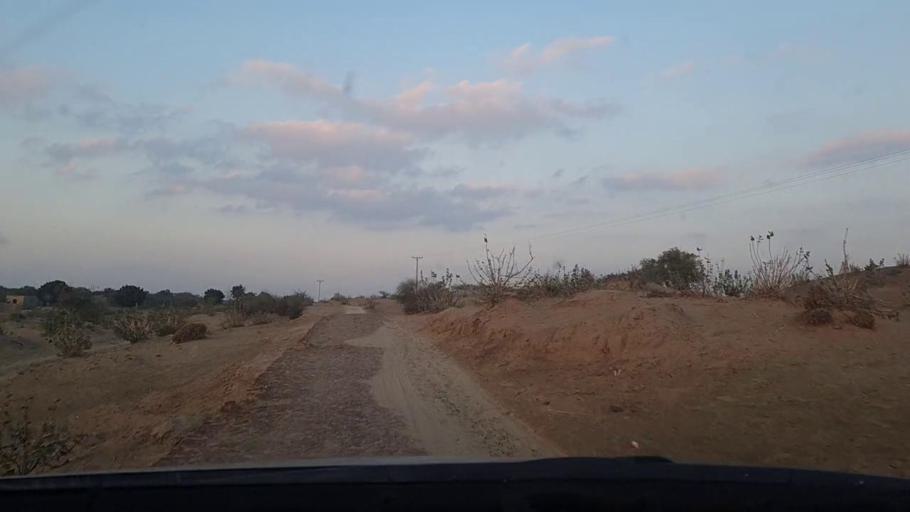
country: PK
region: Sindh
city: Tando Mittha Khan
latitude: 25.9509
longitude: 69.3410
